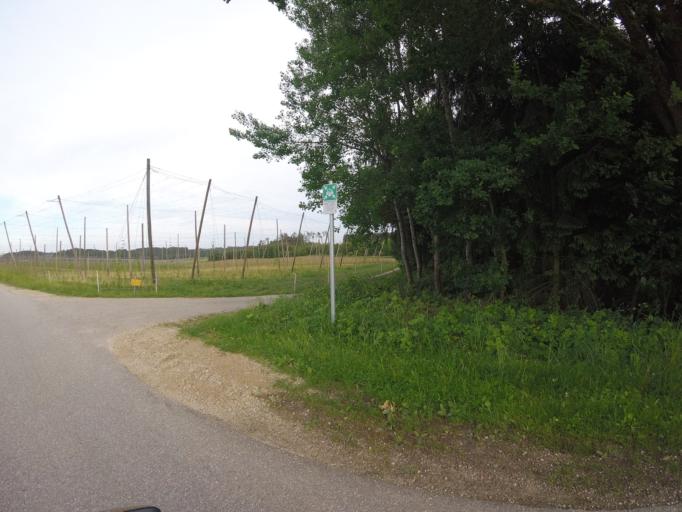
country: DE
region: Bavaria
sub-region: Upper Bavaria
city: Paunzhausen
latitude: 48.4945
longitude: 11.5704
